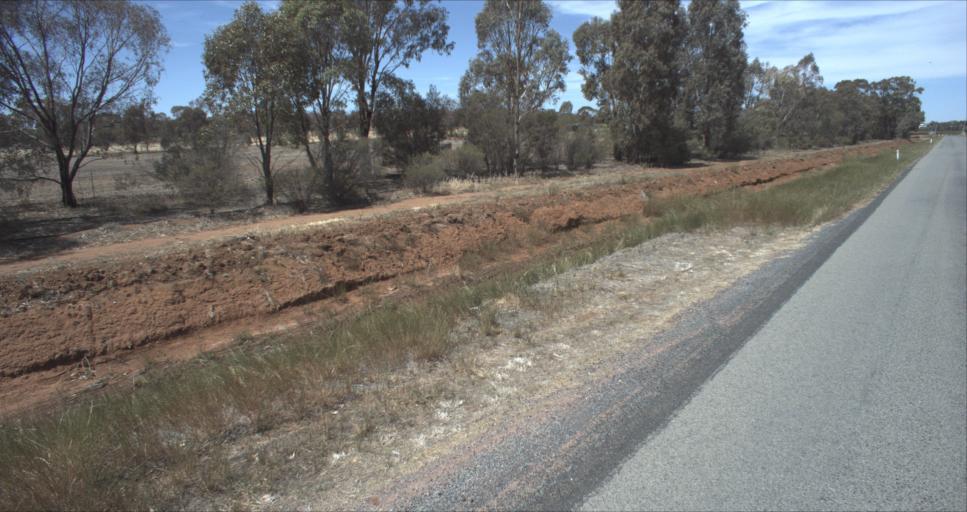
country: AU
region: New South Wales
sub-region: Leeton
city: Leeton
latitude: -34.5582
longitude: 146.4533
